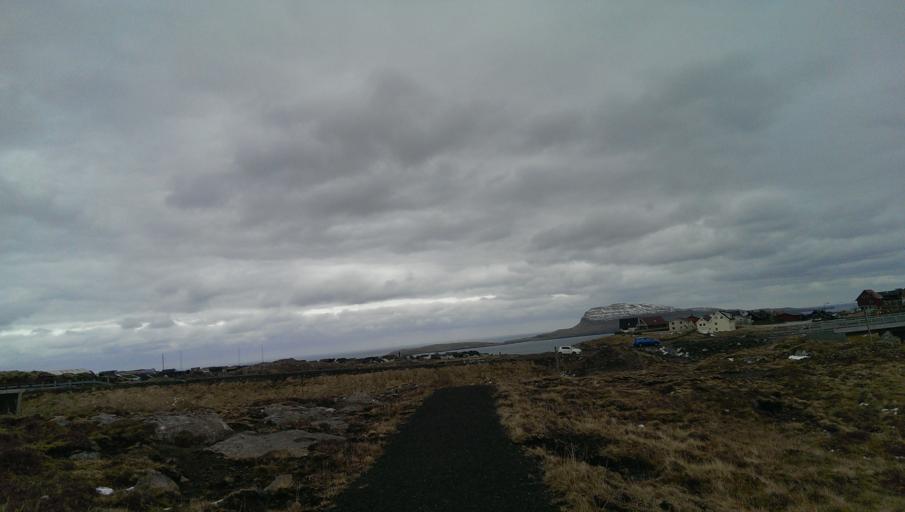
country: FO
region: Streymoy
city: Hoyvik
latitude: 62.0328
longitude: -6.7983
